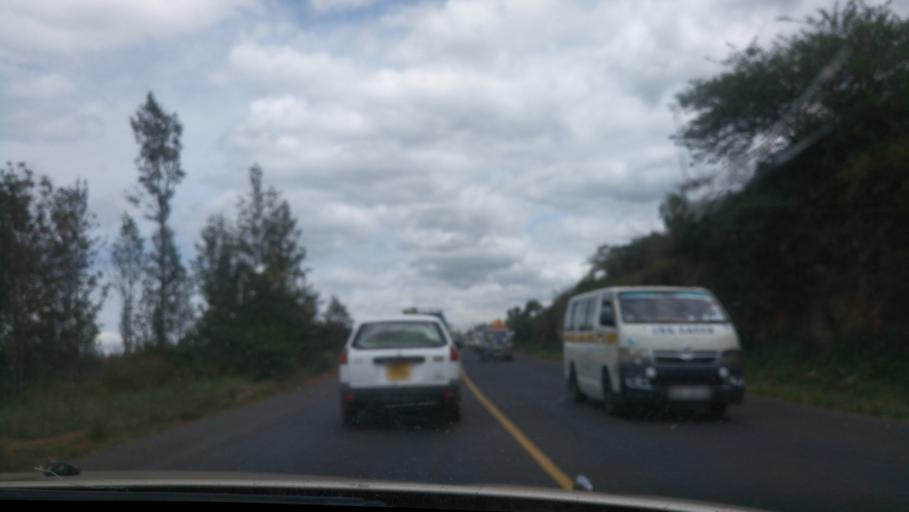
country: KE
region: Murang'a District
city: Maragua
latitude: -0.8503
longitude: 37.2330
